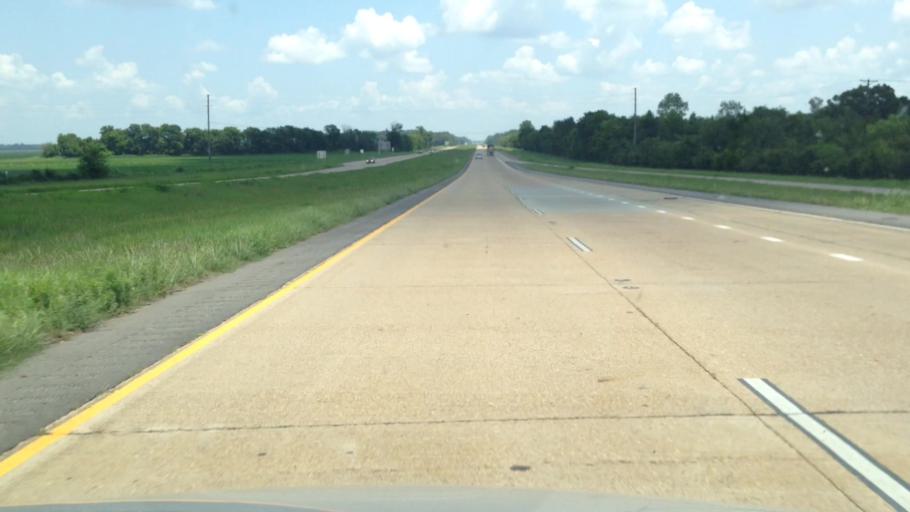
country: US
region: Louisiana
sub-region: Rapides Parish
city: Lecompte
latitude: 31.0136
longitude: -92.3738
